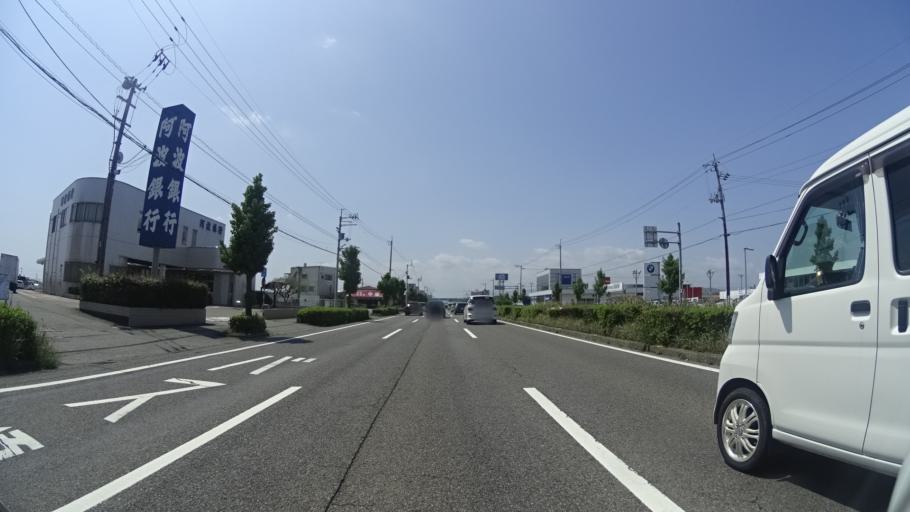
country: JP
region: Tokushima
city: Tokushima-shi
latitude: 34.1151
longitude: 134.5778
